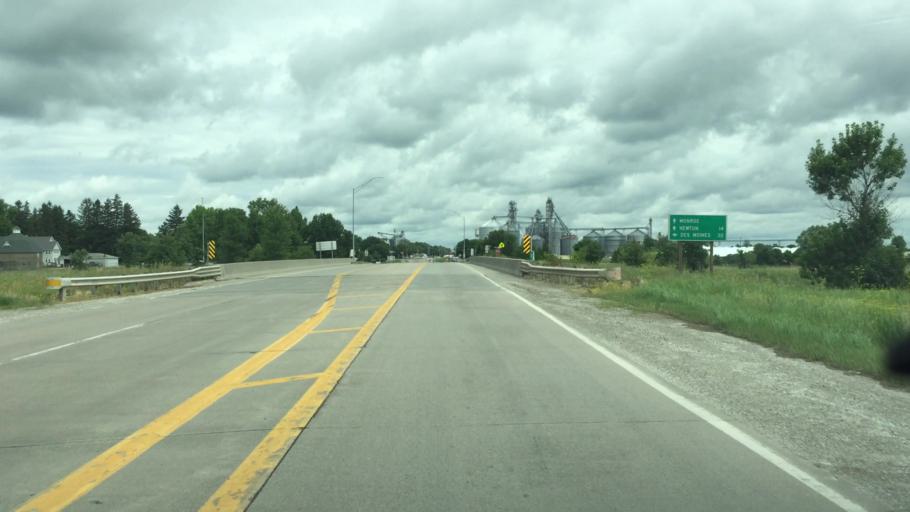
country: US
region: Iowa
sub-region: Jasper County
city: Monroe
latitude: 41.5107
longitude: -93.1011
